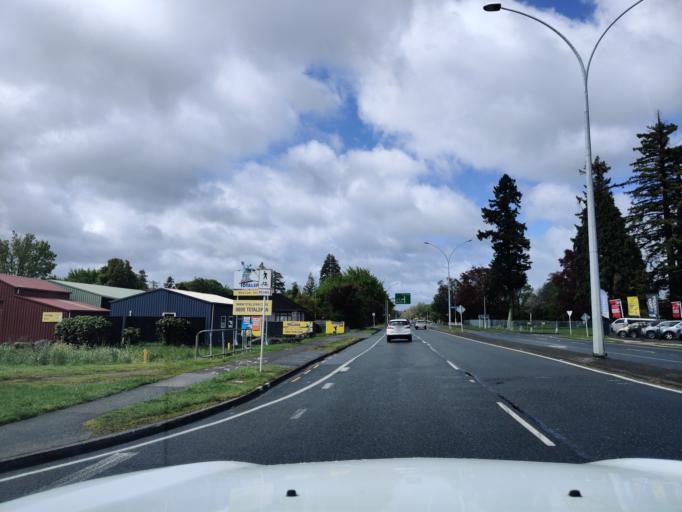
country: NZ
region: Bay of Plenty
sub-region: Rotorua District
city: Rotorua
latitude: -38.1344
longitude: 176.2346
